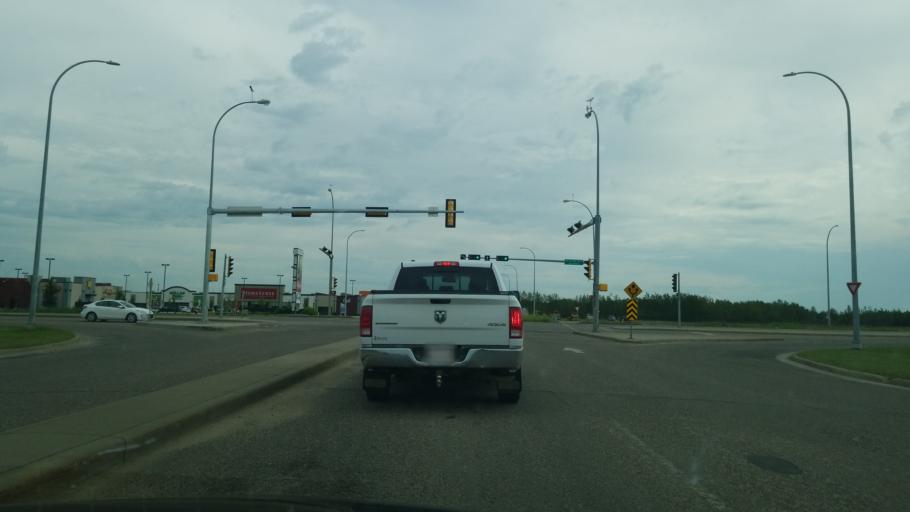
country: CA
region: Saskatchewan
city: Lloydminster
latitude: 53.2785
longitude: -110.0631
